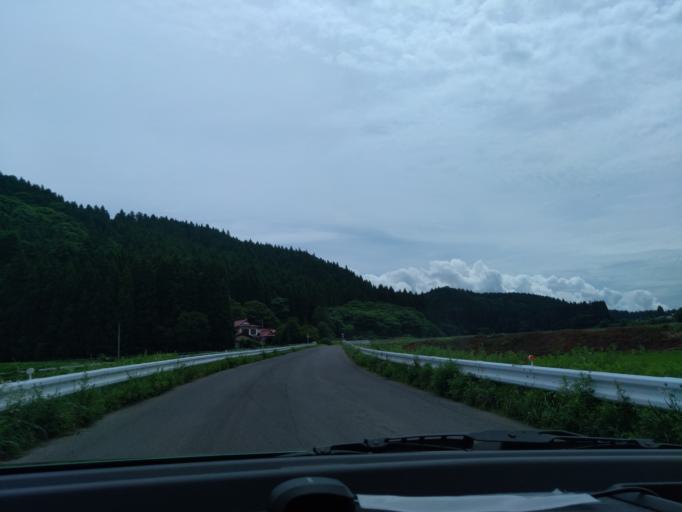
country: JP
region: Akita
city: Kakunodatemachi
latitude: 39.5951
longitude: 140.6177
